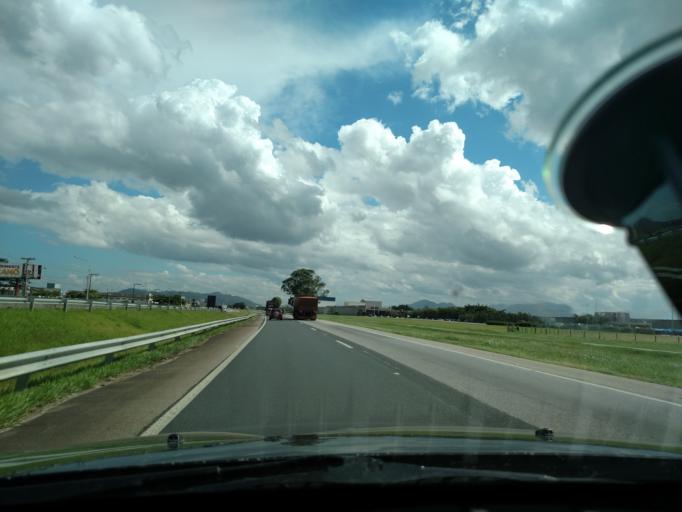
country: BR
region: Santa Catarina
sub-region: Tijucas
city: Tijucas
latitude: -27.2184
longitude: -48.6252
